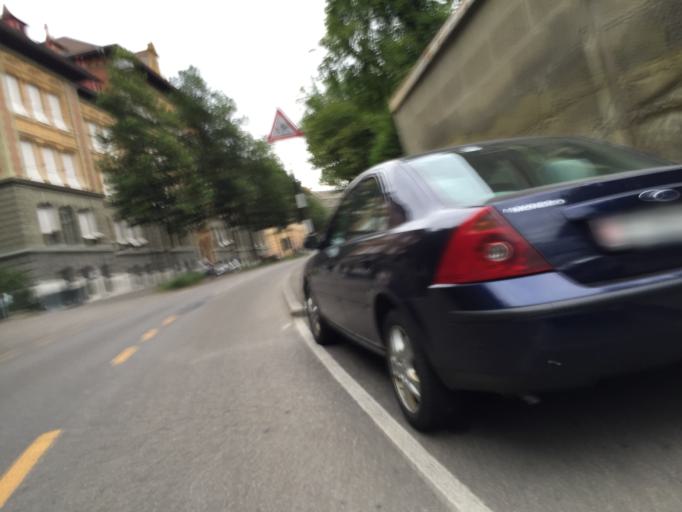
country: CH
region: Bern
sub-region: Bern-Mittelland District
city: Bern
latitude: 46.9430
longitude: 7.4376
